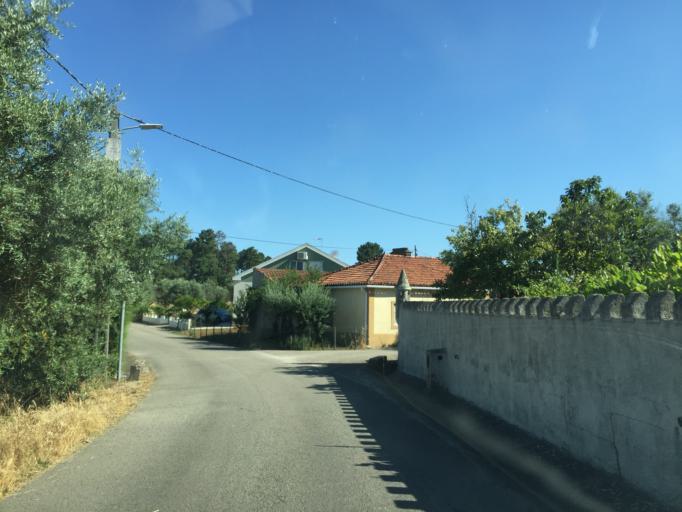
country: PT
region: Santarem
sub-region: Tomar
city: Tomar
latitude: 39.6027
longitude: -8.3267
